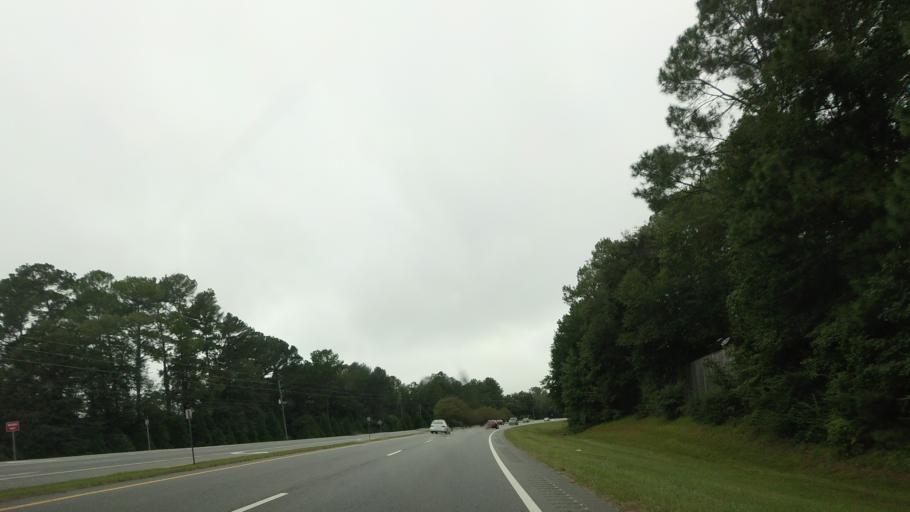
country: US
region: Georgia
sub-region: Lowndes County
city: Remerton
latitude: 30.8807
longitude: -83.3081
